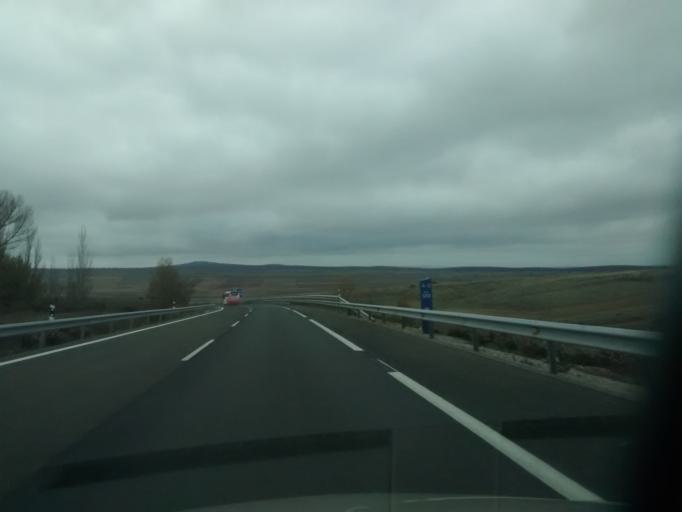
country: ES
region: Castille-La Mancha
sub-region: Provincia de Guadalajara
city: Torremocha del Campo
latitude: 40.9908
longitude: -2.5959
